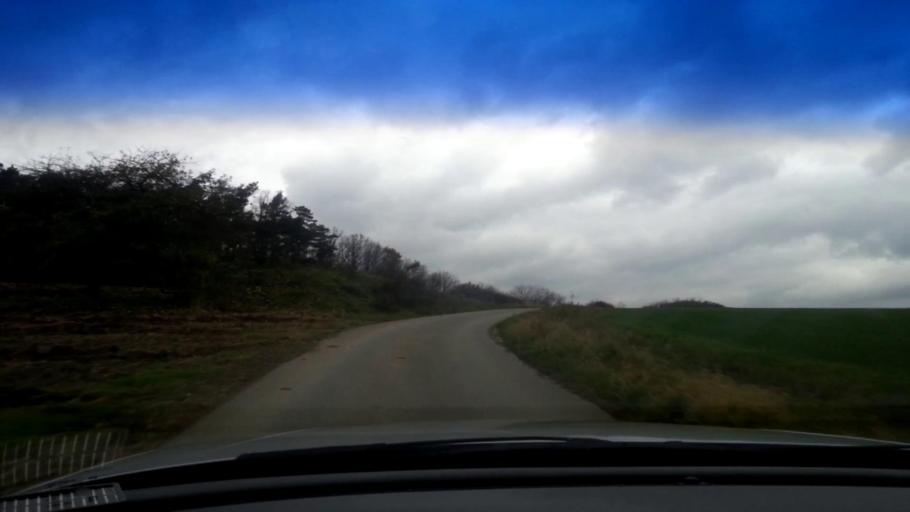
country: DE
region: Bavaria
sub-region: Upper Franconia
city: Walsdorf
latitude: 49.8579
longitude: 10.7944
